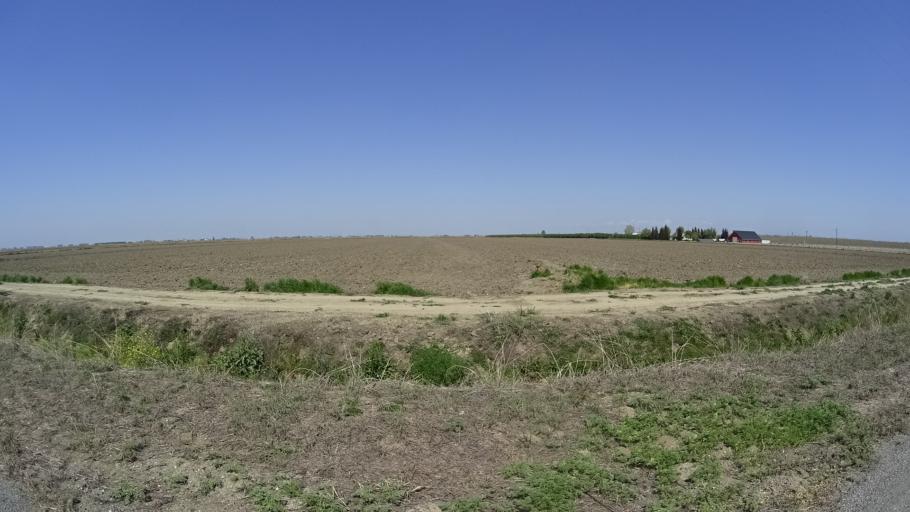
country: US
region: California
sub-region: Glenn County
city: Willows
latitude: 39.5288
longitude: -122.0307
